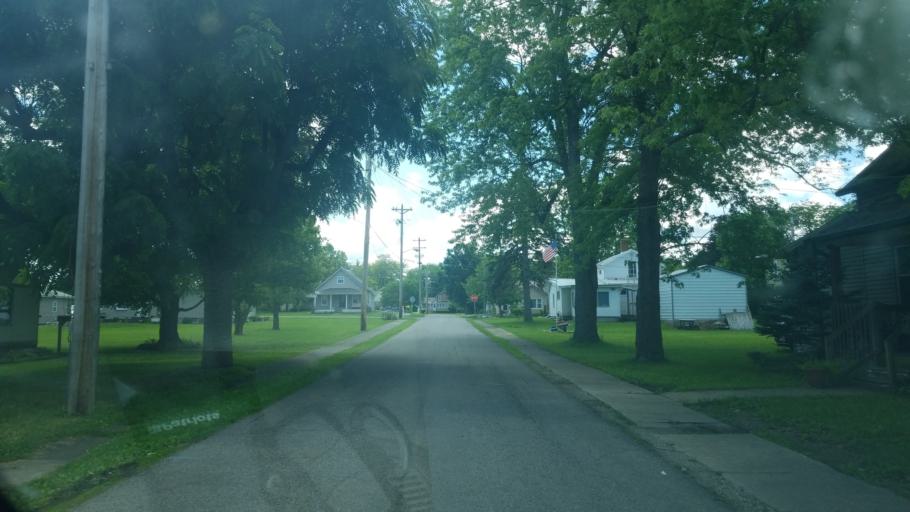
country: US
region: Ohio
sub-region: Huron County
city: New London
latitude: 41.0838
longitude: -82.3917
